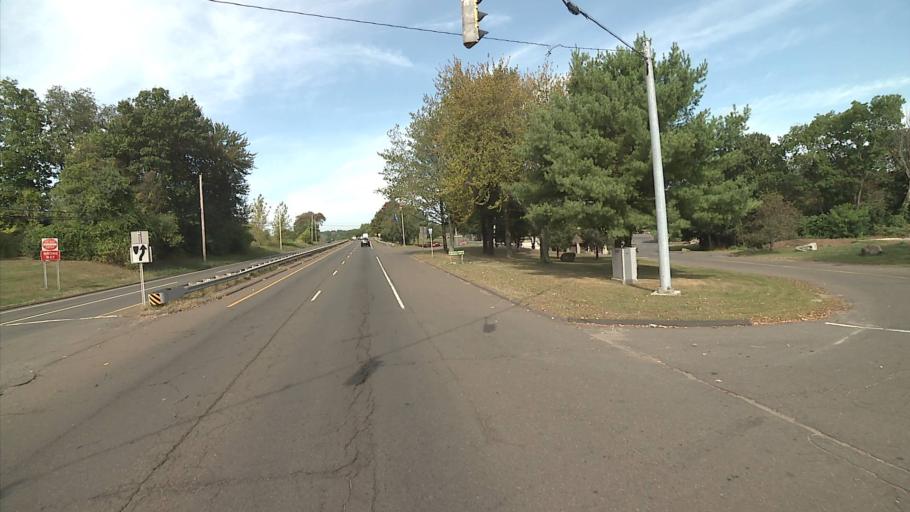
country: US
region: Connecticut
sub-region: New Haven County
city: Orange
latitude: 41.3090
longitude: -73.0381
